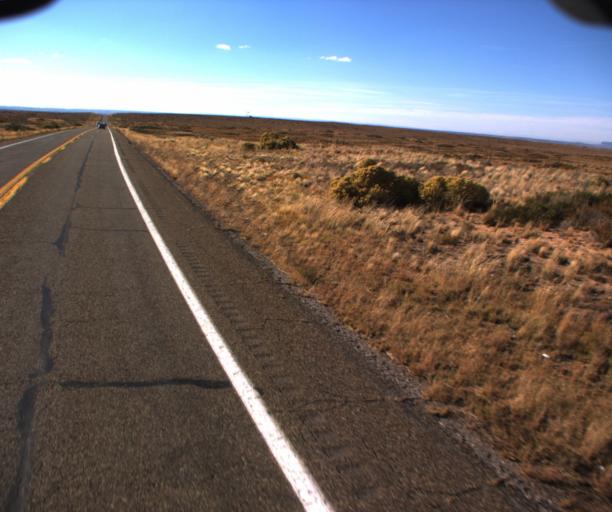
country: US
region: Arizona
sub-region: Coconino County
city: Kaibito
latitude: 36.6120
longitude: -111.0161
